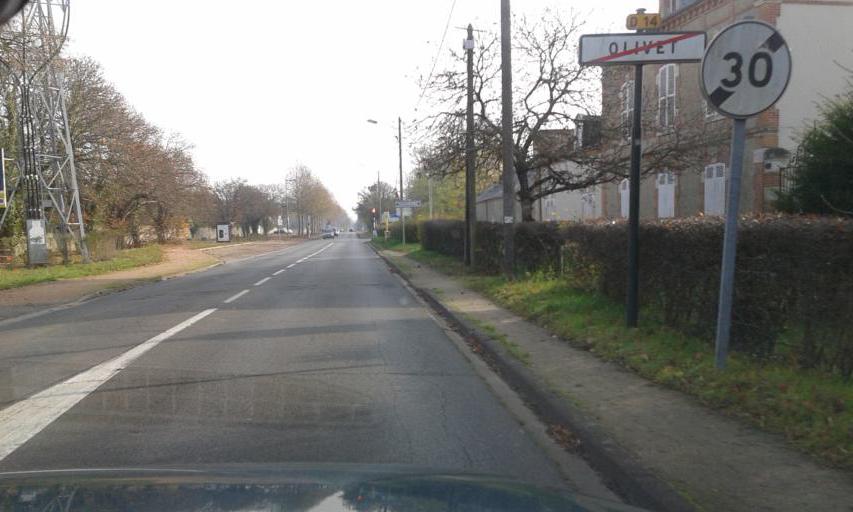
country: FR
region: Centre
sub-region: Departement du Loiret
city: Olivet
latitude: 47.8506
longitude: 1.9282
